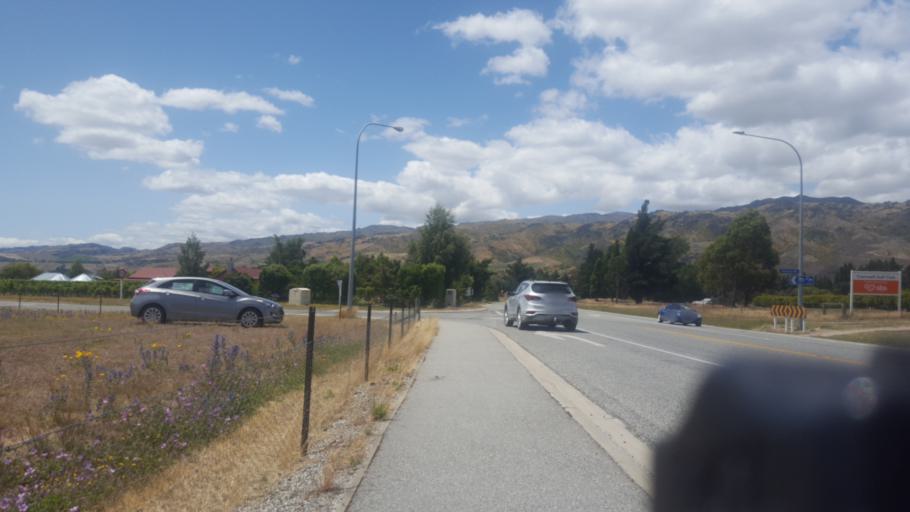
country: NZ
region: Otago
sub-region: Queenstown-Lakes District
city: Wanaka
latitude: -45.0345
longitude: 169.2017
